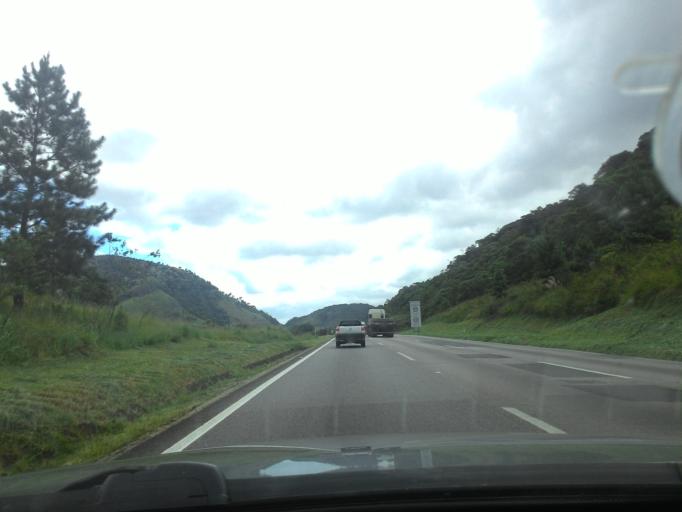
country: BR
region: Sao Paulo
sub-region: Cajati
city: Cajati
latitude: -24.8868
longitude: -48.2288
